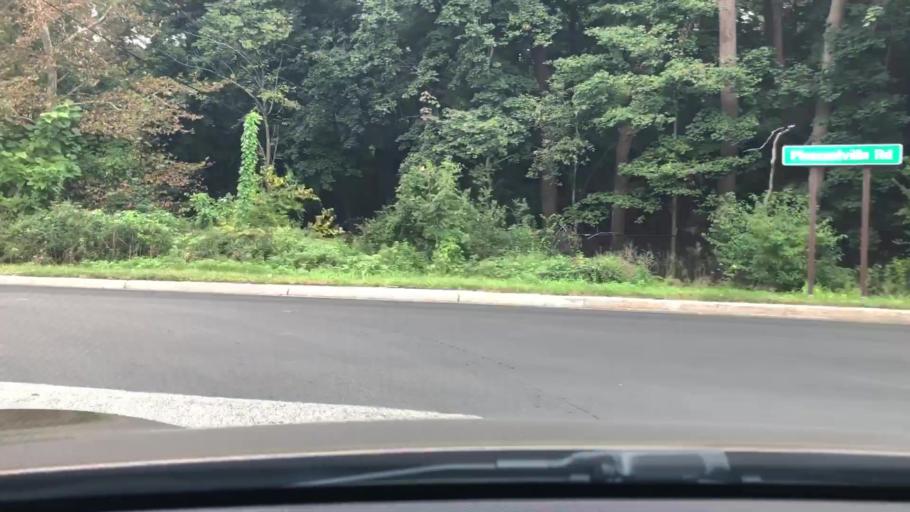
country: US
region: New York
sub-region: Westchester County
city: Briarcliff Manor
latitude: 41.1428
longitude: -73.8140
